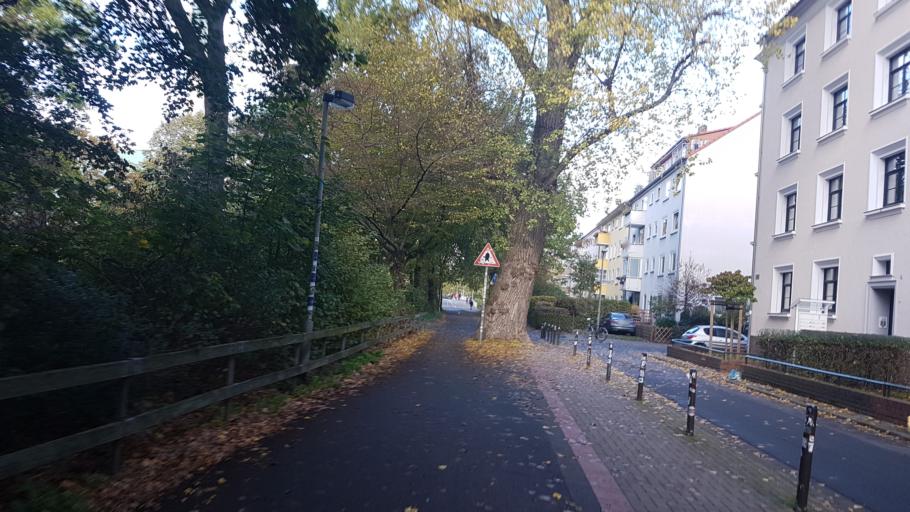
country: DE
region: Lower Saxony
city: Hannover
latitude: 52.3767
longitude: 9.7082
